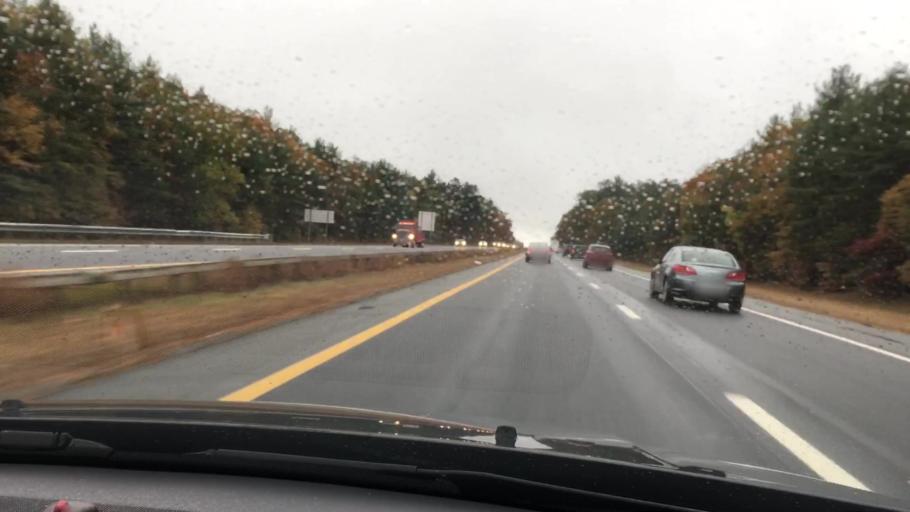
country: US
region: New Hampshire
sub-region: Hillsborough County
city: Litchfield
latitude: 42.8038
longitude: -71.4988
